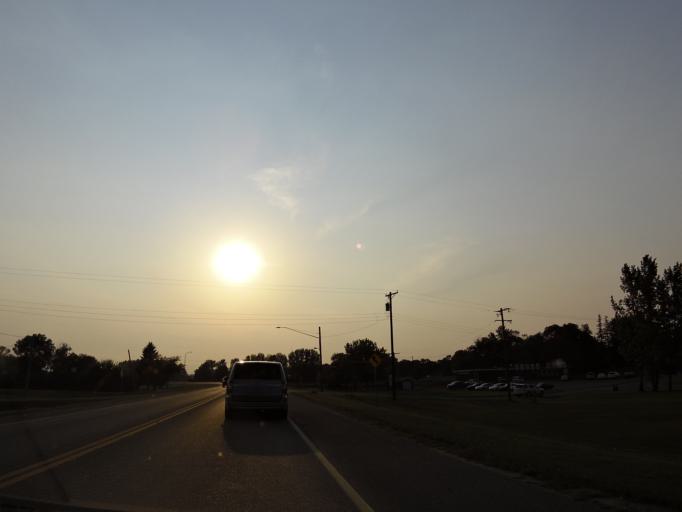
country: US
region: North Dakota
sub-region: Traill County
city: Mayville
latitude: 47.4981
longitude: -97.3274
